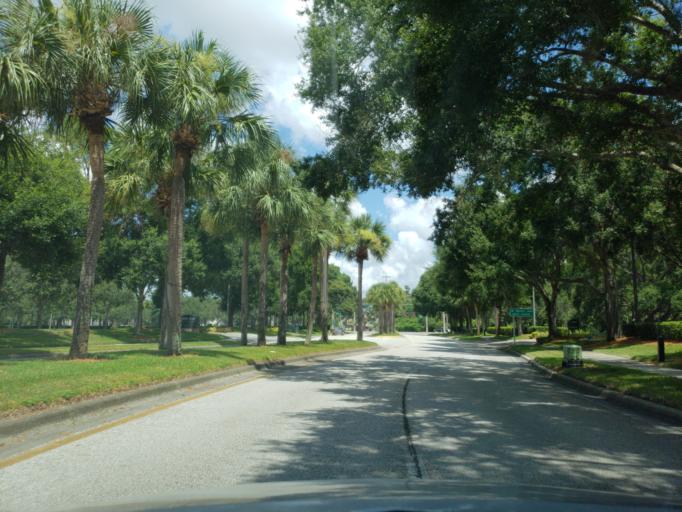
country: US
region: Florida
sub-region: Hillsborough County
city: Egypt Lake-Leto
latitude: 28.0237
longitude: -82.5219
